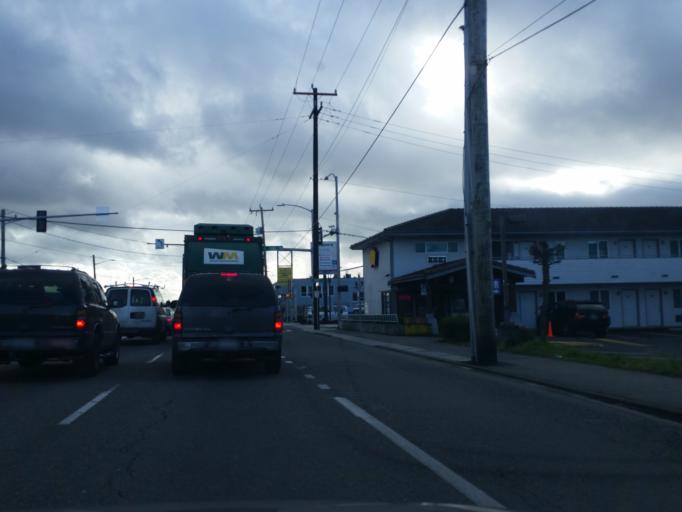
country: US
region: Washington
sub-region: King County
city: Shoreline
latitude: 47.6983
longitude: -122.3447
